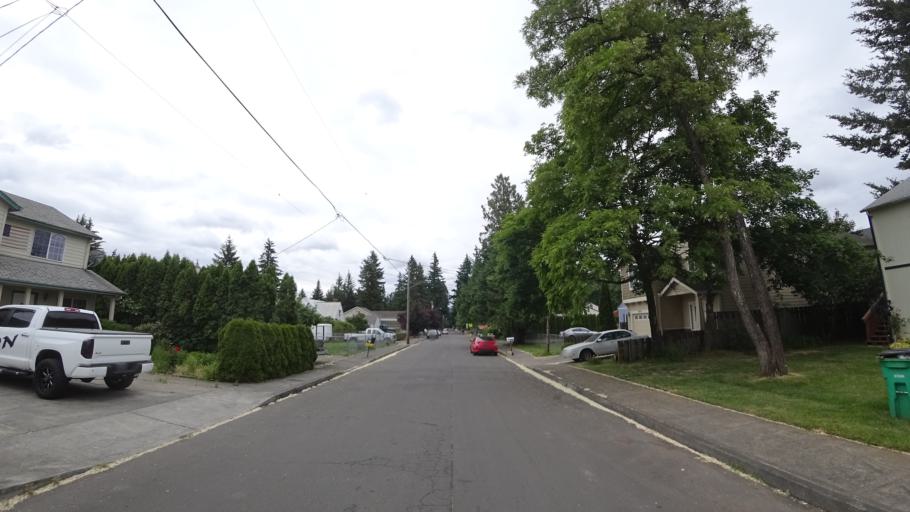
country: US
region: Oregon
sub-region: Multnomah County
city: Lents
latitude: 45.5027
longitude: -122.5422
